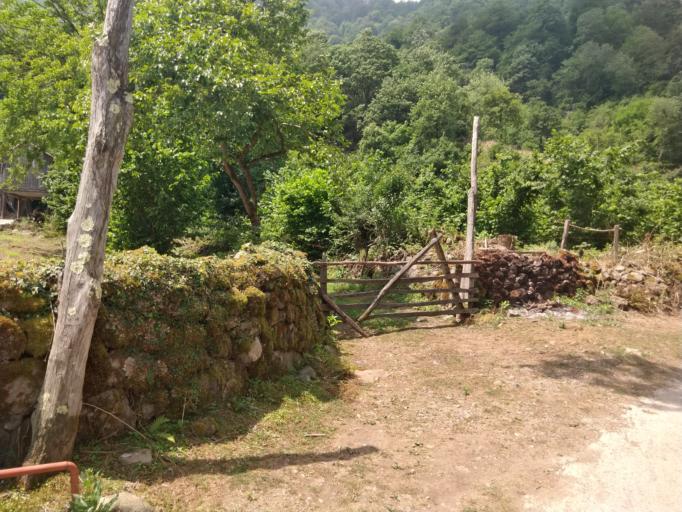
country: TR
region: Artvin
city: Muratli
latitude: 41.5281
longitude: 41.7136
